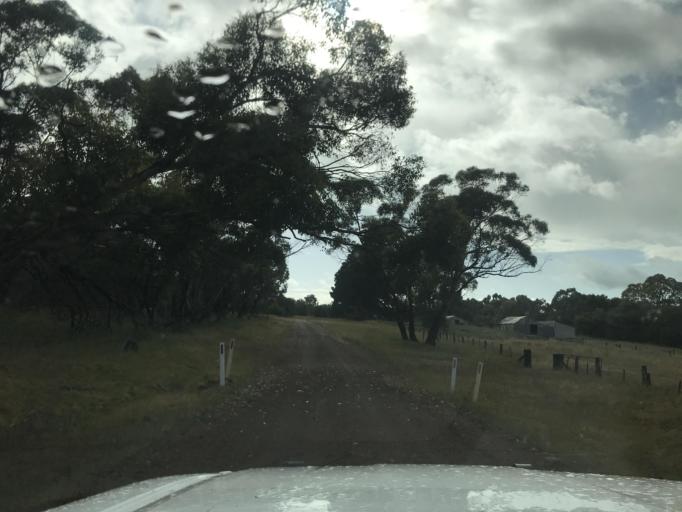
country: AU
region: South Australia
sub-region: Wattle Range
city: Penola
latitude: -37.2209
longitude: 141.2912
